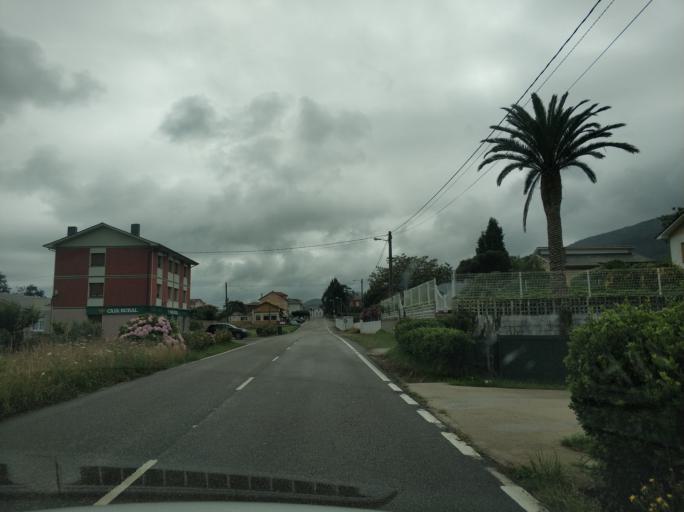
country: ES
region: Asturias
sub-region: Province of Asturias
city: Salas
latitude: 43.5447
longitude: -6.3919
